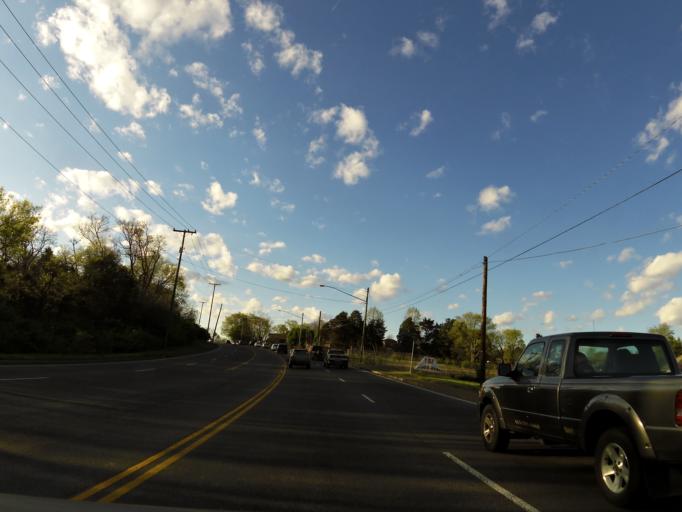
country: US
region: Tennessee
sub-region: Davidson County
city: Lakewood
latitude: 36.2324
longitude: -86.6247
